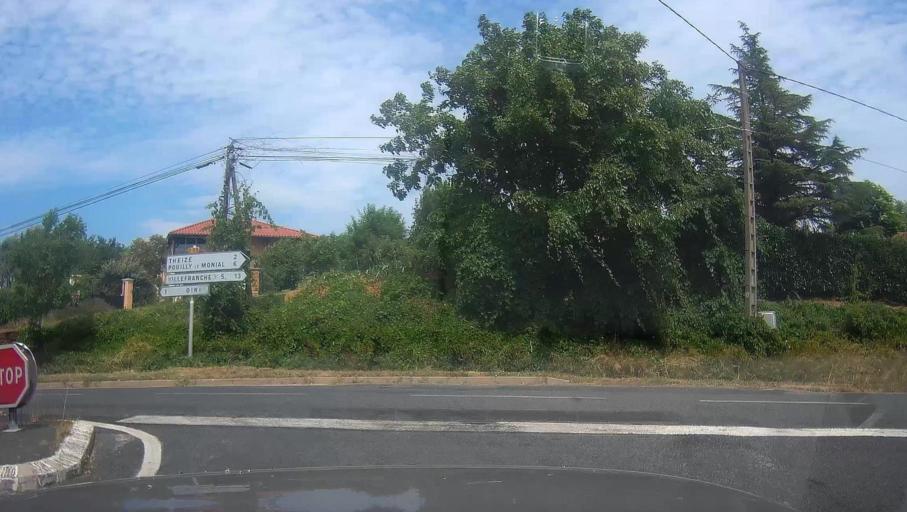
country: FR
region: Rhone-Alpes
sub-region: Departement du Rhone
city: Theize
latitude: 45.9482
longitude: 4.5895
